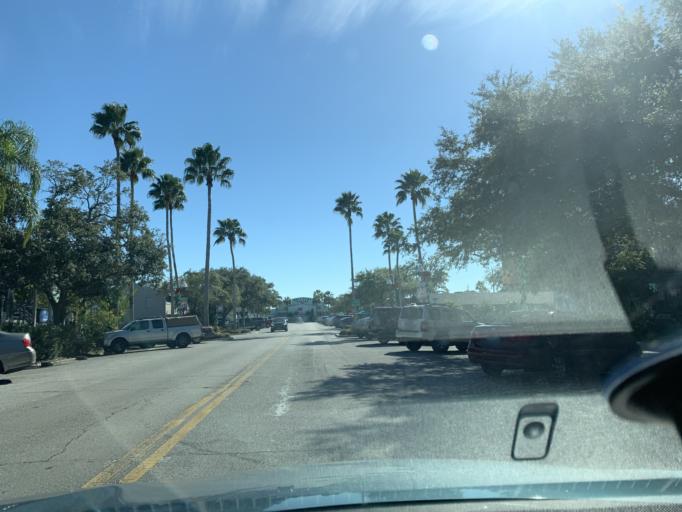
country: US
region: Florida
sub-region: Pinellas County
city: Gulfport
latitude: 27.7393
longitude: -82.7079
